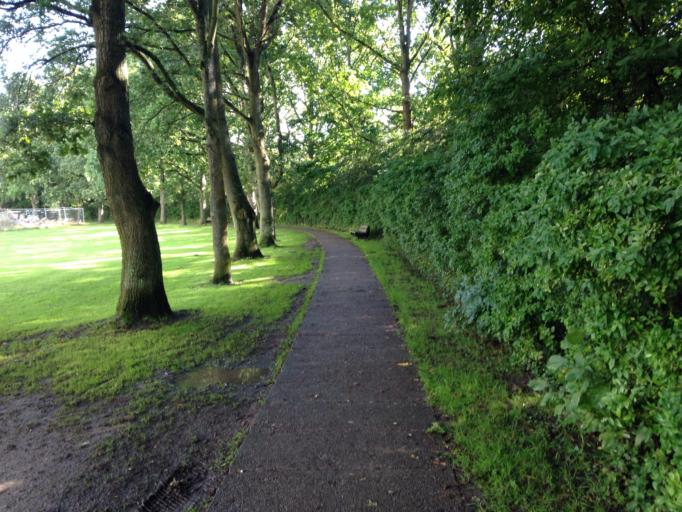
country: DK
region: Capital Region
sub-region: Glostrup Kommune
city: Glostrup
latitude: 55.6690
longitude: 12.3896
